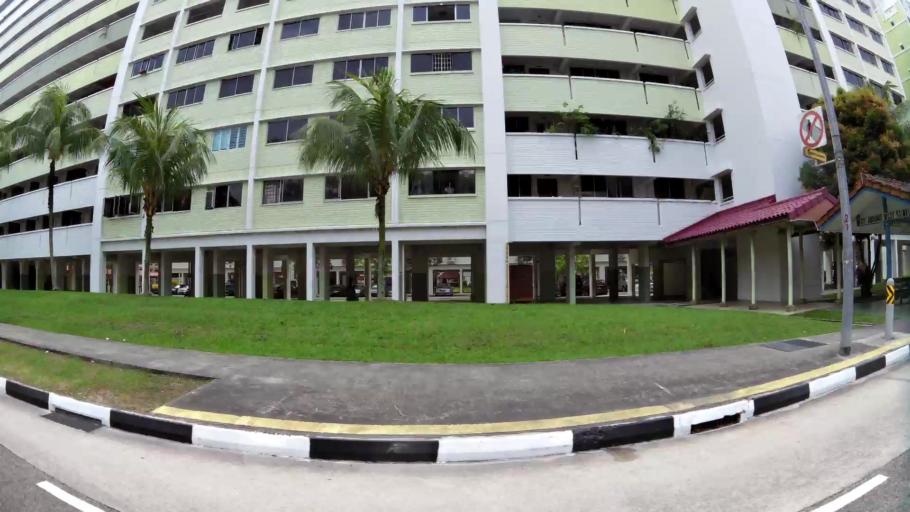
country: MY
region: Johor
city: Johor Bahru
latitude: 1.3471
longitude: 103.6943
